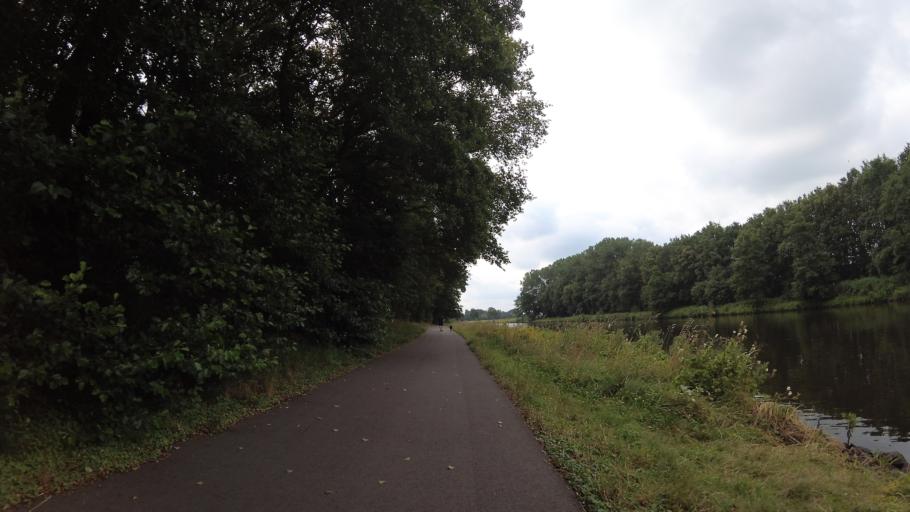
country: DE
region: Lower Saxony
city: Lathen
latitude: 52.8569
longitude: 7.3016
